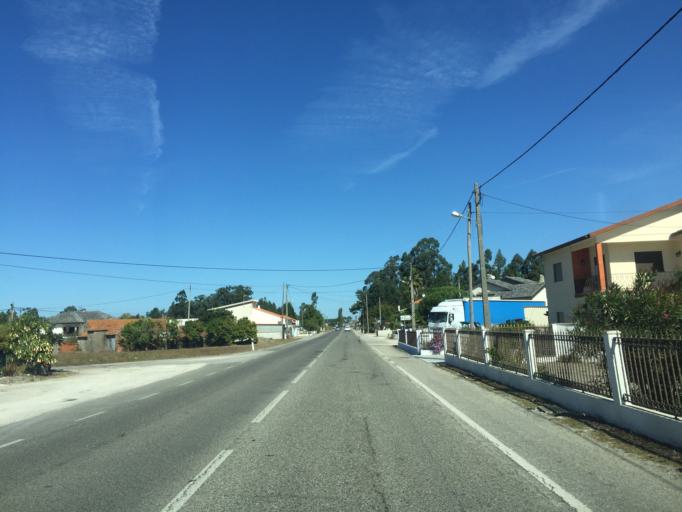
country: PT
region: Coimbra
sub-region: Figueira da Foz
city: Alhadas
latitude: 40.2447
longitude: -8.7893
